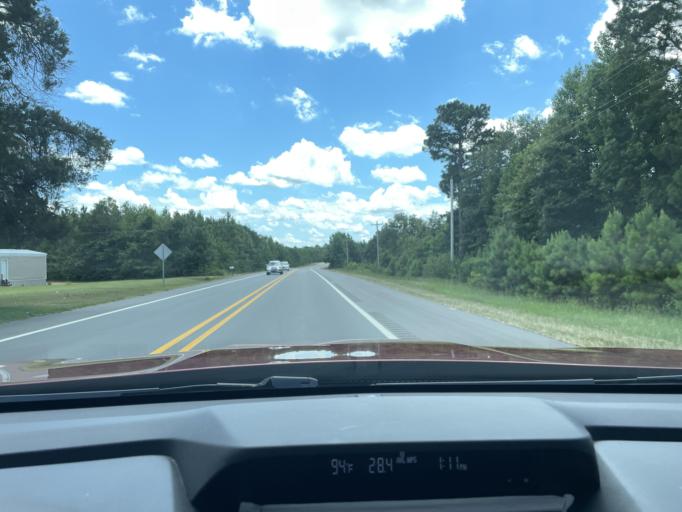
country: US
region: Arkansas
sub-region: Drew County
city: Monticello
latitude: 33.7123
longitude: -91.8098
